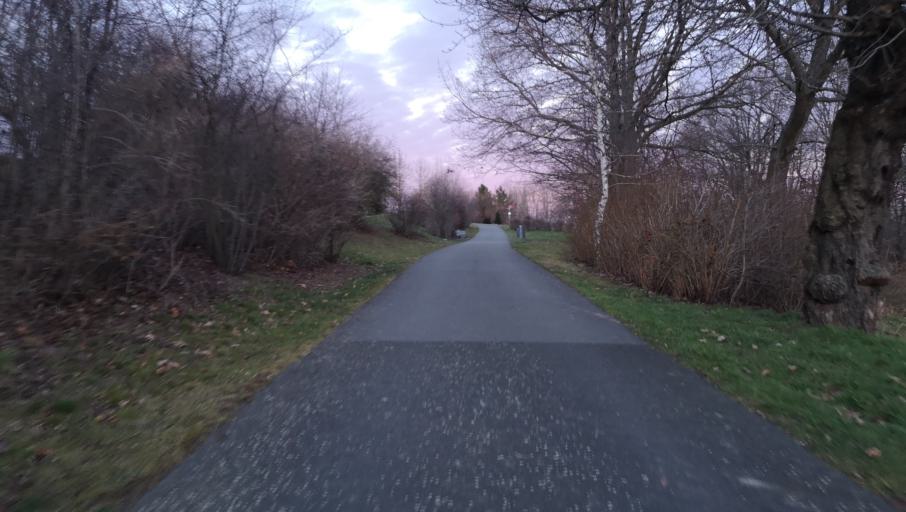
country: DE
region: Thuringia
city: Ronneburg
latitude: 50.8596
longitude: 12.1679
